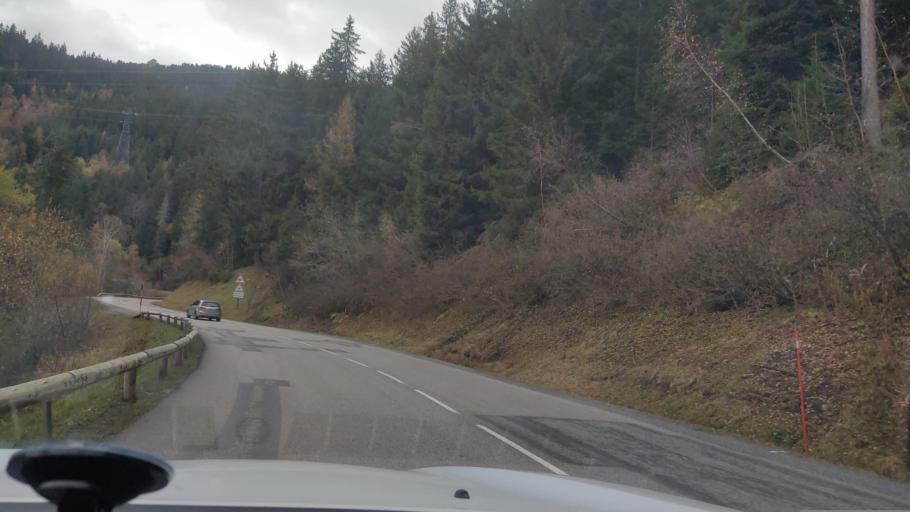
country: FR
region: Rhone-Alpes
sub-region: Departement de la Savoie
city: Bourg-Saint-Maurice
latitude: 45.5832
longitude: 6.7805
